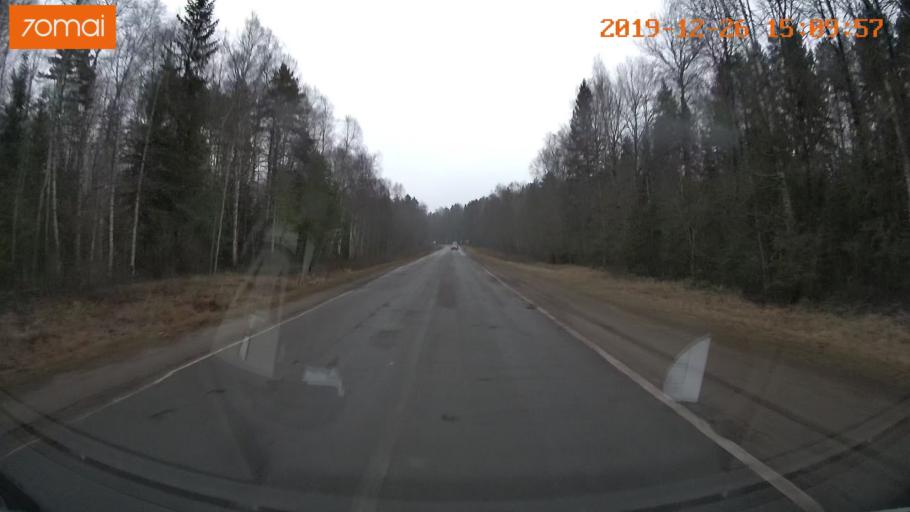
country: RU
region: Jaroslavl
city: Rybinsk
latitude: 58.1445
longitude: 38.8460
